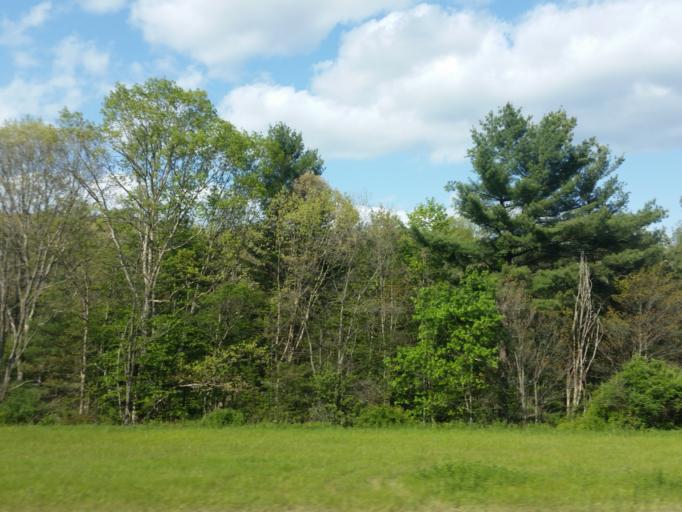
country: US
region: West Virginia
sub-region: Raleigh County
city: Shady Spring
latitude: 37.6783
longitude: -81.1218
